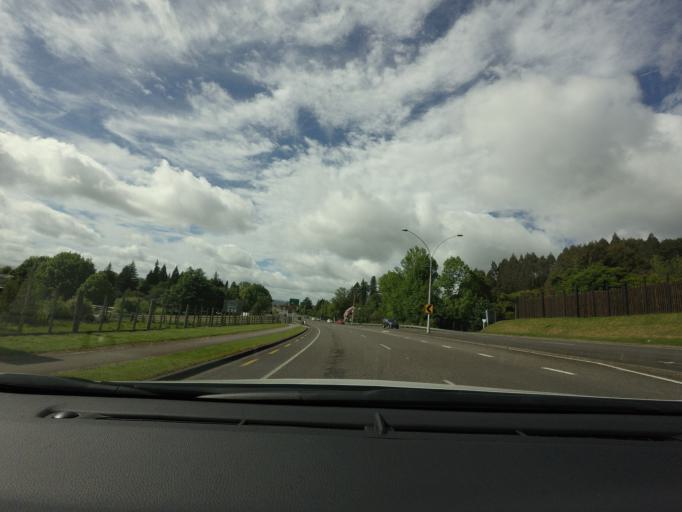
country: NZ
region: Bay of Plenty
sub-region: Rotorua District
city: Rotorua
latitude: -38.1067
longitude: 176.2216
